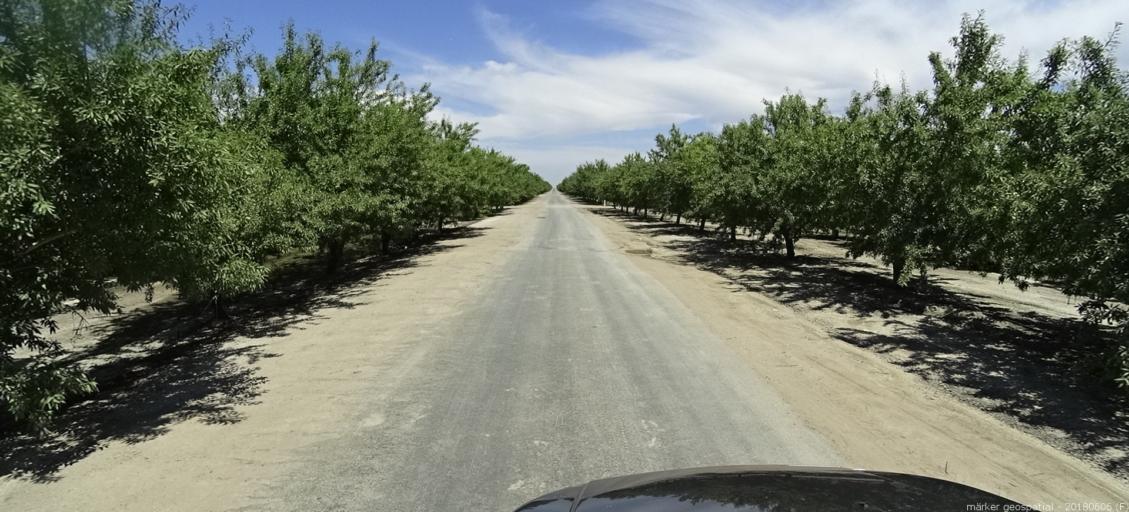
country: US
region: California
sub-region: Fresno County
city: Firebaugh
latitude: 36.8723
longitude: -120.3999
